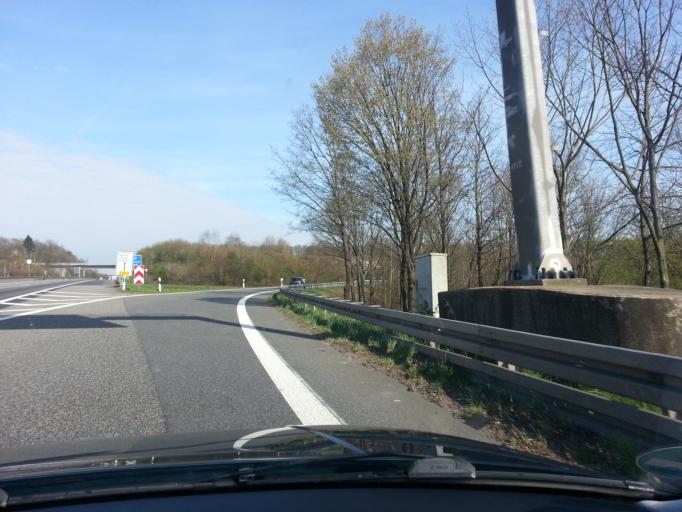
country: DE
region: Saarland
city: Friedrichsthal
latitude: 49.3184
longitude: 7.0829
